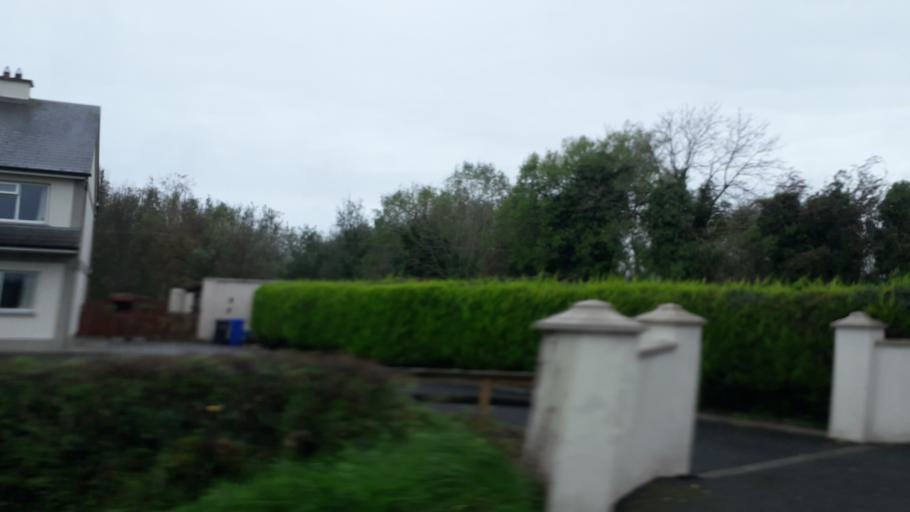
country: IE
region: Connaught
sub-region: Roscommon
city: Ballaghaderreen
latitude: 53.8873
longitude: -8.5396
